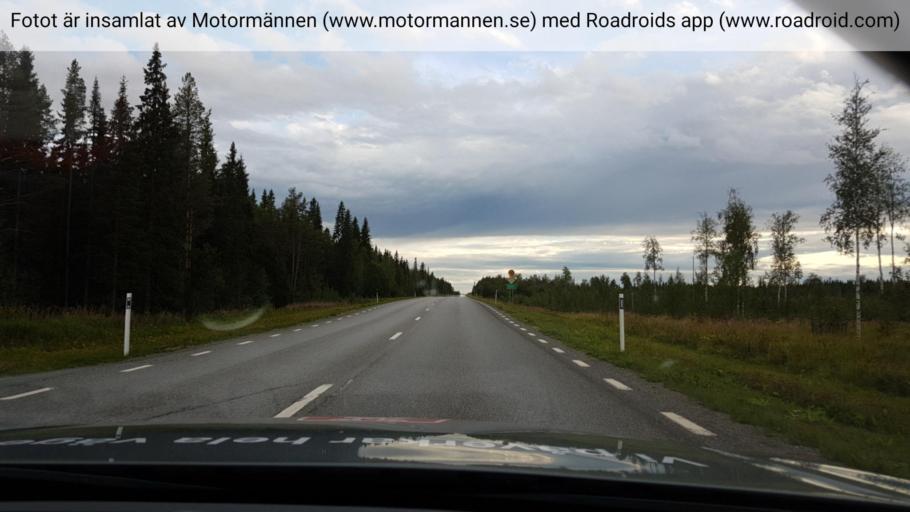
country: SE
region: Jaemtland
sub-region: Stroemsunds Kommun
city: Stroemsund
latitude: 63.7171
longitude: 15.4676
